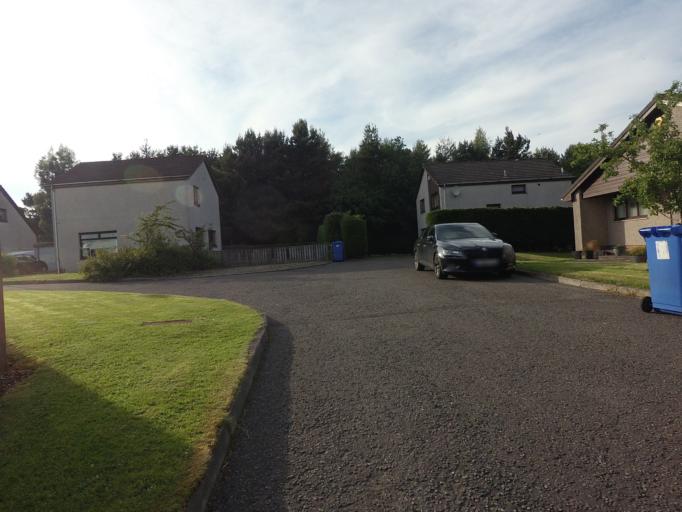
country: GB
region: Scotland
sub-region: West Lothian
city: Livingston
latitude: 55.9079
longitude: -3.5424
